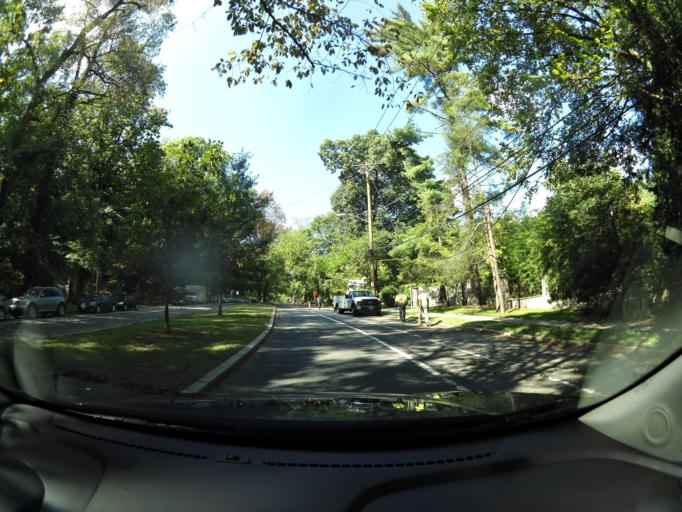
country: US
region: Maryland
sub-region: Montgomery County
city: Chevy Chase Village
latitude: 38.9410
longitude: -77.0562
